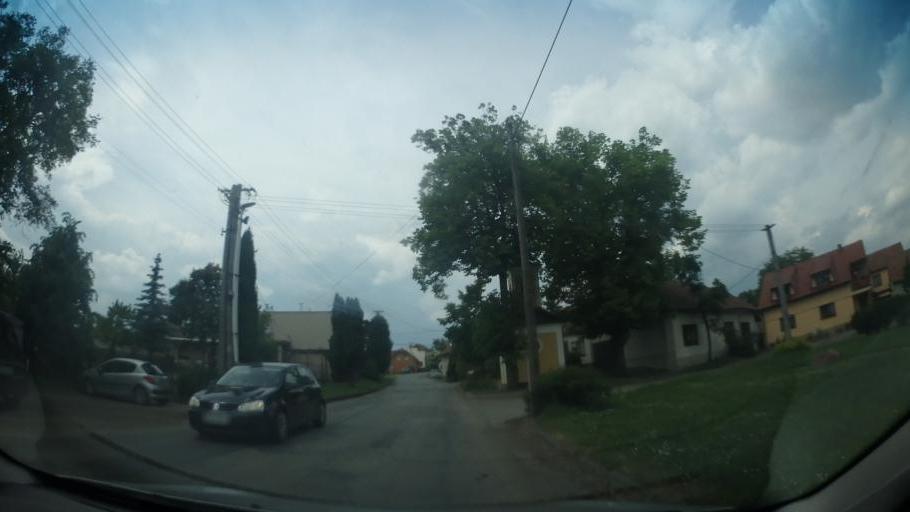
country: CZ
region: South Moravian
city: Lysice
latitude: 49.4522
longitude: 16.5063
